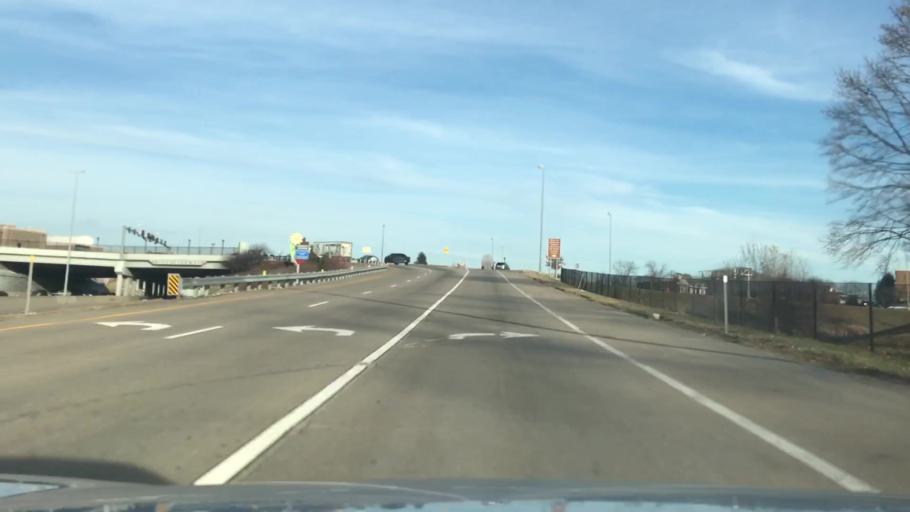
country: US
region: Missouri
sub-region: Saint Louis County
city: University City
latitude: 38.6300
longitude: -90.2673
